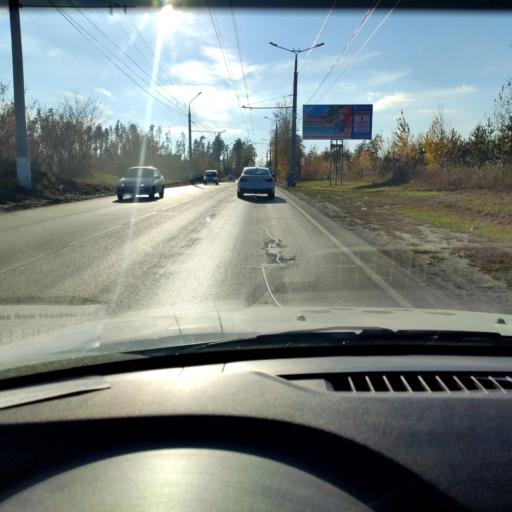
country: RU
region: Samara
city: Tol'yatti
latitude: 53.4813
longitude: 49.3758
